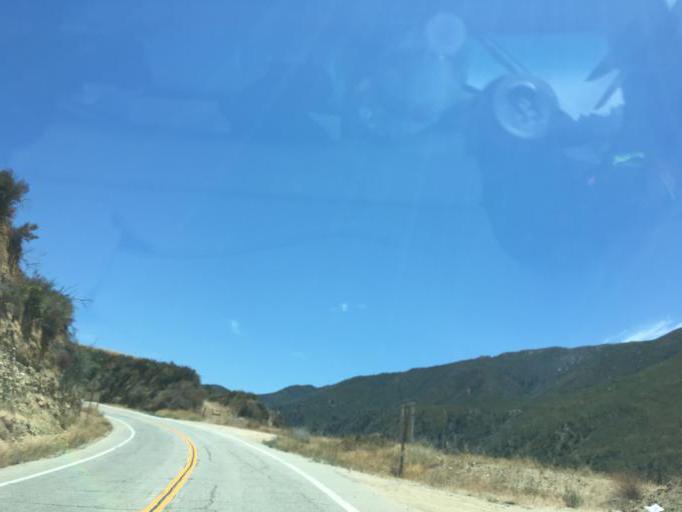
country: US
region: California
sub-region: Los Angeles County
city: La Crescenta-Montrose
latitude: 34.2881
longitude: -118.2254
